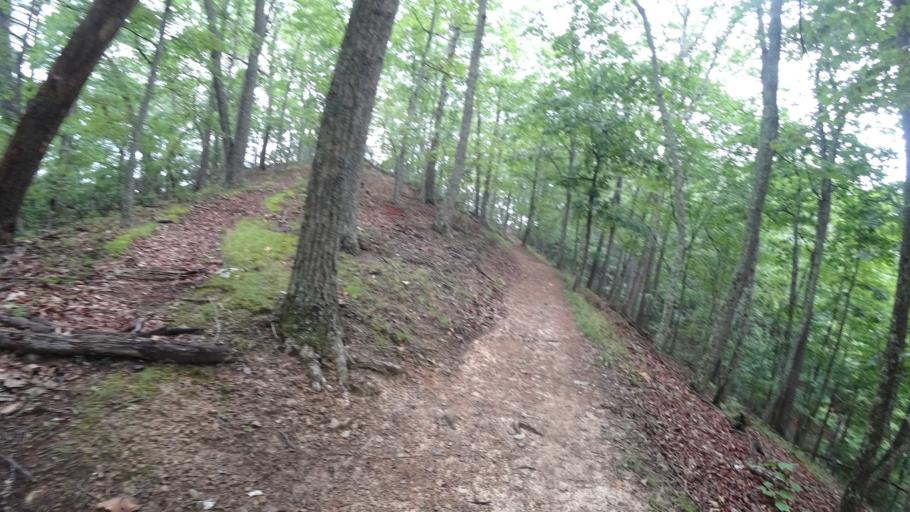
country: US
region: Virginia
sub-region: Smyth County
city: Marion
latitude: 36.8848
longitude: -81.5197
